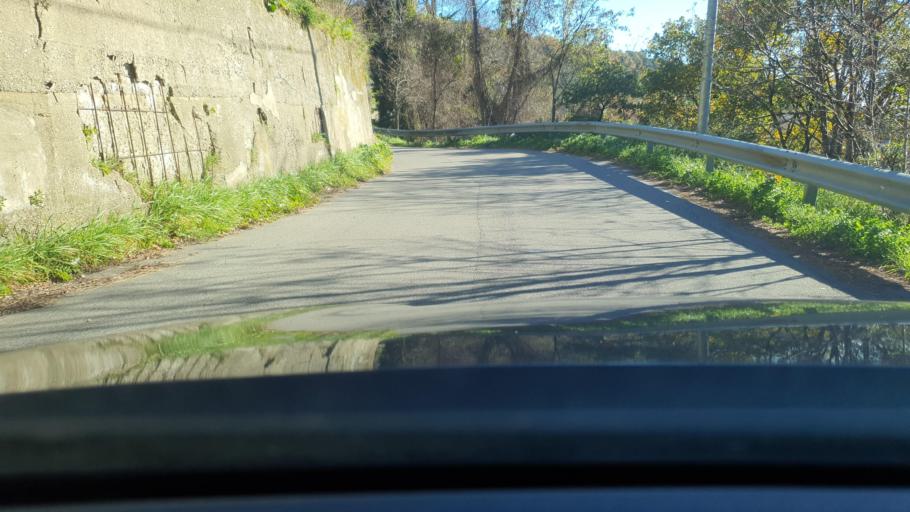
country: IT
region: Calabria
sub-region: Provincia di Catanzaro
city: Sant'Elia
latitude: 38.9573
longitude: 16.5797
